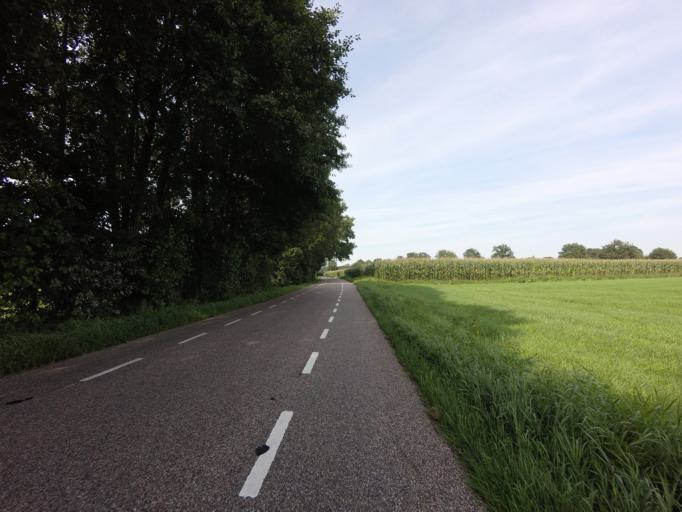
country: NL
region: Overijssel
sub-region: Gemeente Tubbergen
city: Tubbergen
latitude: 52.4180
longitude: 6.7759
